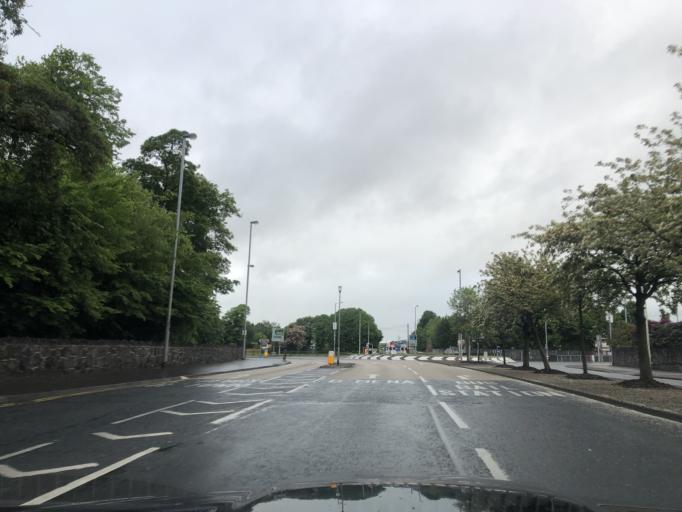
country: GB
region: Northern Ireland
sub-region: Antrim Borough
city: Antrim
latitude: 54.7190
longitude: -6.2208
